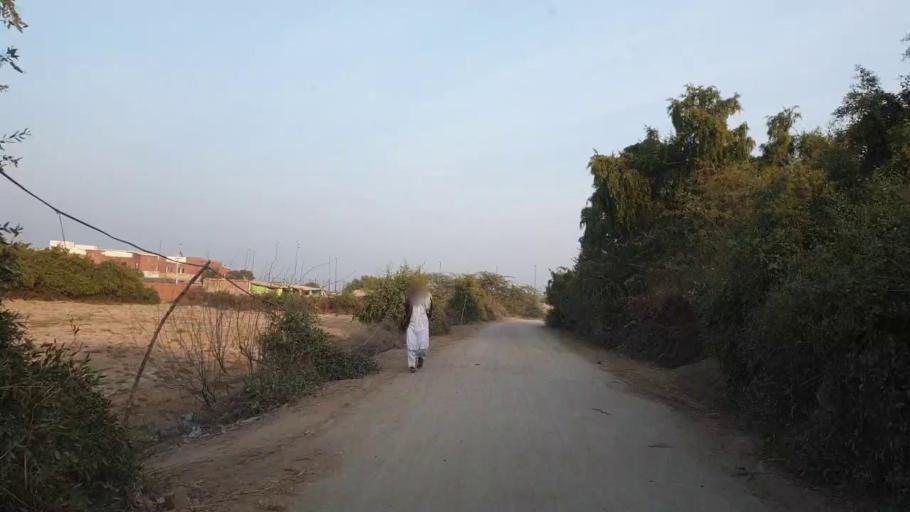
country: PK
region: Sindh
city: Matiari
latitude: 25.6069
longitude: 68.4324
